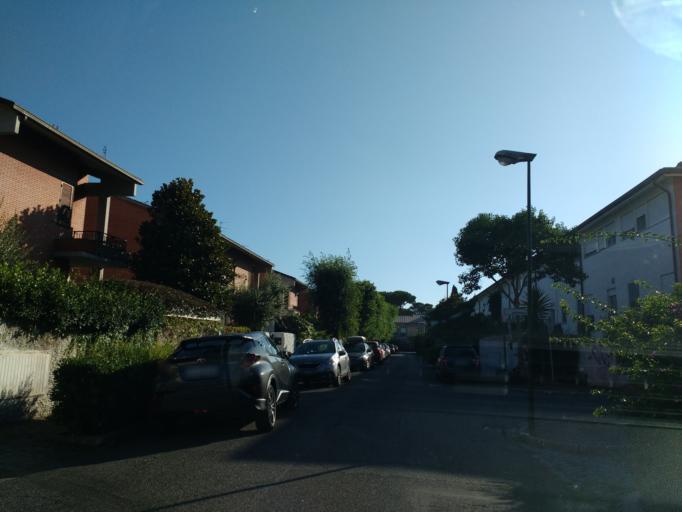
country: IT
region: Latium
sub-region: Citta metropolitana di Roma Capitale
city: Acilia-Castel Fusano-Ostia Antica
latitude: 41.7543
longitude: 12.3557
